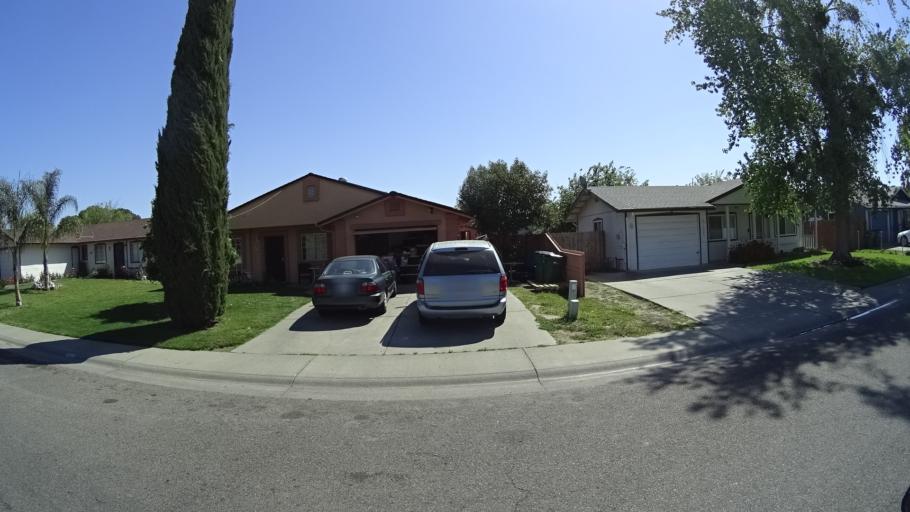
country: US
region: California
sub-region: Glenn County
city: Orland
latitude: 39.7395
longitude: -122.1828
